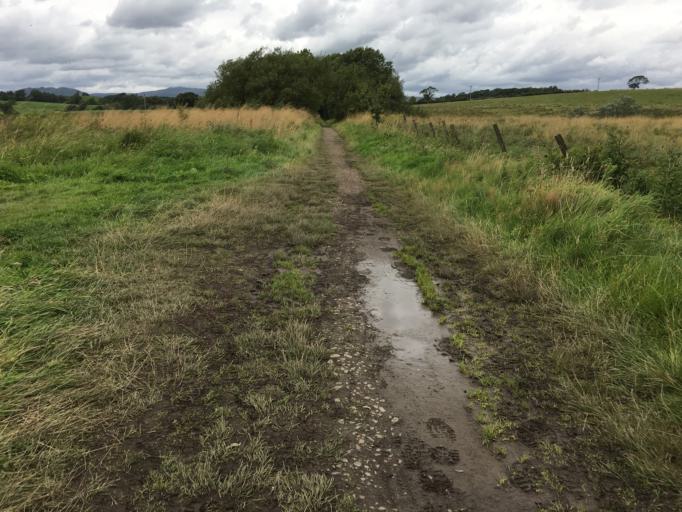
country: GB
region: Scotland
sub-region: Stirling
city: Killearn
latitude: 56.0431
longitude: -4.3964
